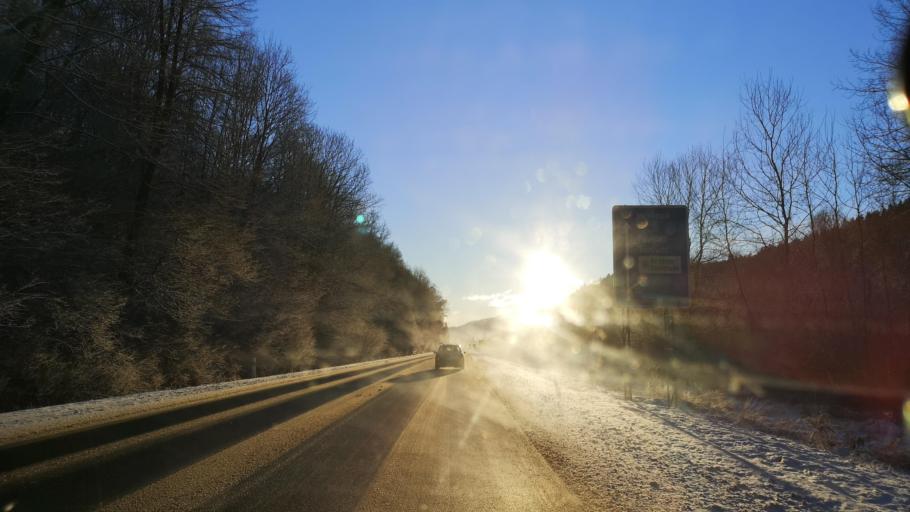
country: SK
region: Banskobystricky
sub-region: Okres Banska Bystrica
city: Brezno
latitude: 48.8110
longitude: 19.6061
